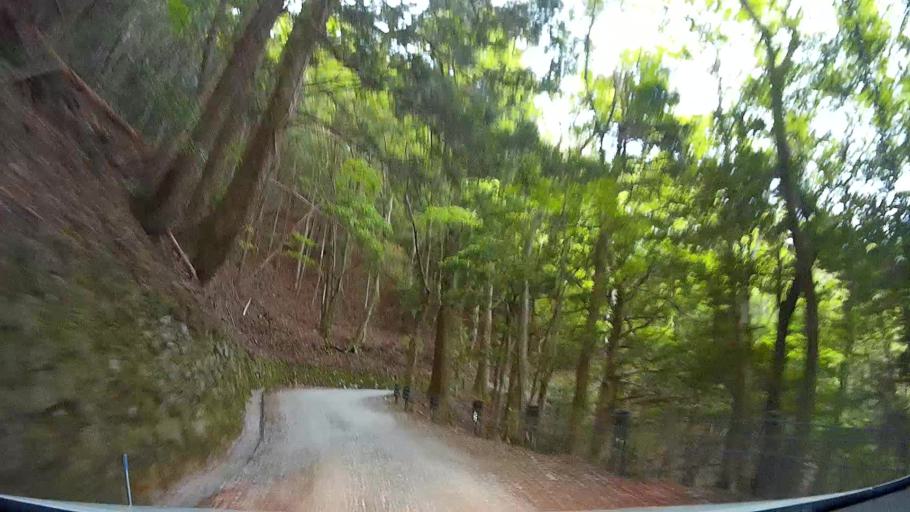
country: JP
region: Shizuoka
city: Shimoda
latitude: 34.8356
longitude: 138.9318
